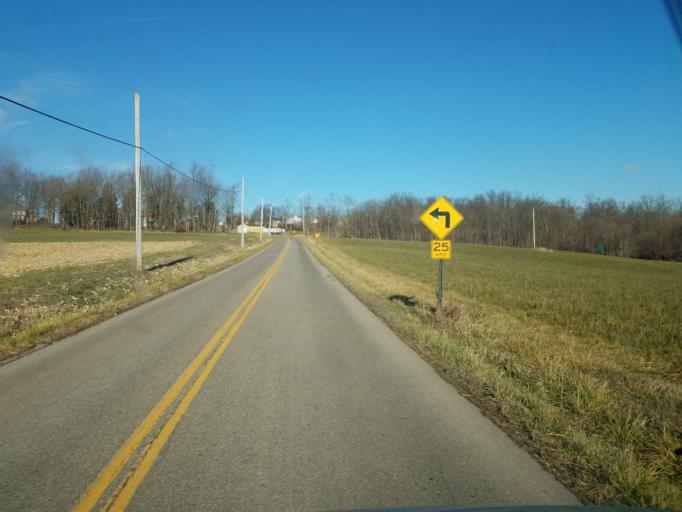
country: US
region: Ohio
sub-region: Stark County
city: Brewster
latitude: 40.7216
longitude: -81.6656
